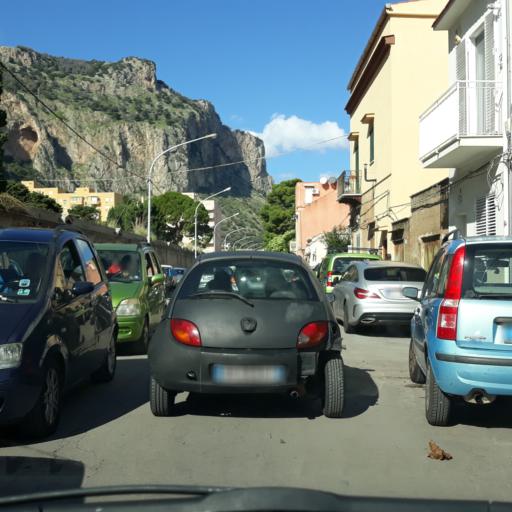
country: IT
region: Sicily
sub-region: Palermo
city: Palermo
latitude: 38.1625
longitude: 13.3703
